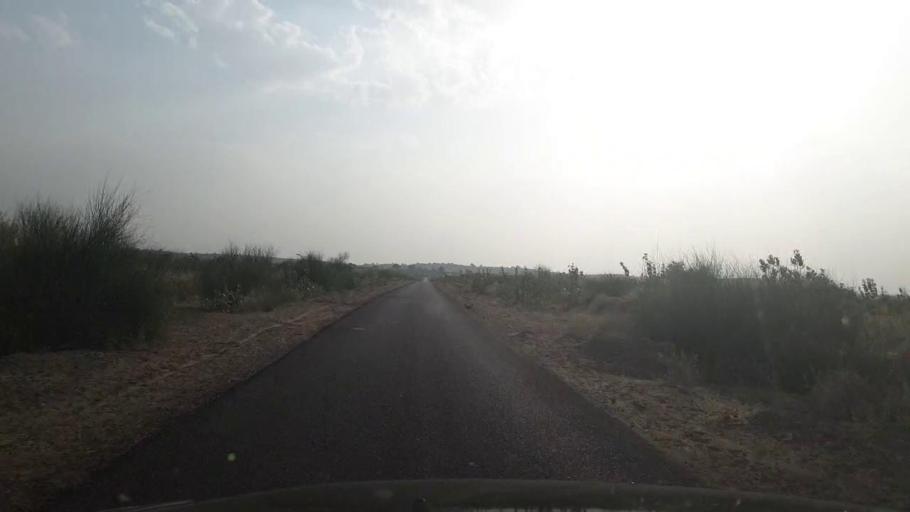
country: PK
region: Sindh
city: Islamkot
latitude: 25.0630
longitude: 70.4610
